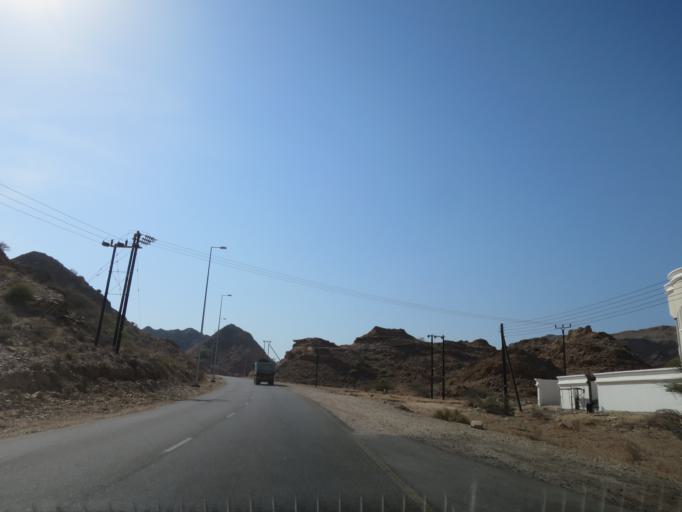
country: OM
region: Muhafazat Masqat
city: Muscat
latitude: 23.5161
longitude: 58.7141
